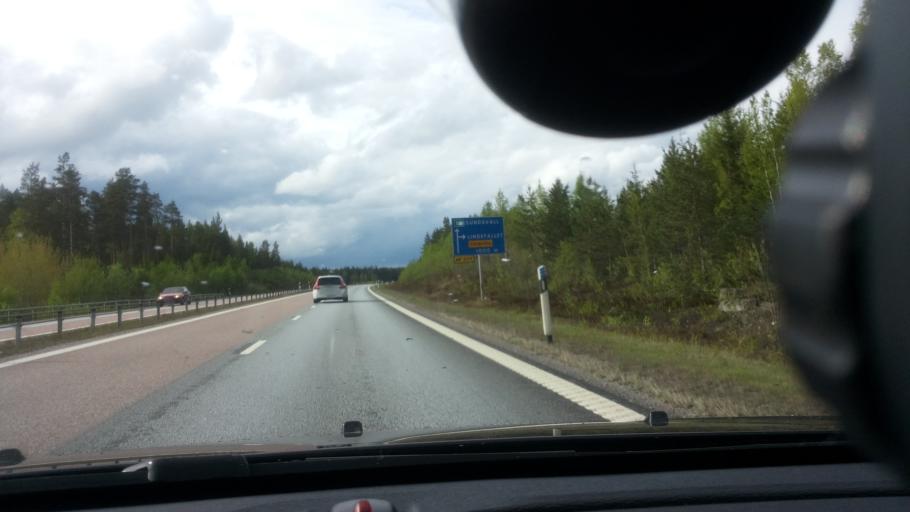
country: SE
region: Gaevleborg
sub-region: Soderhamns Kommun
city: Soderhamn
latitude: 61.4162
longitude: 16.9884
